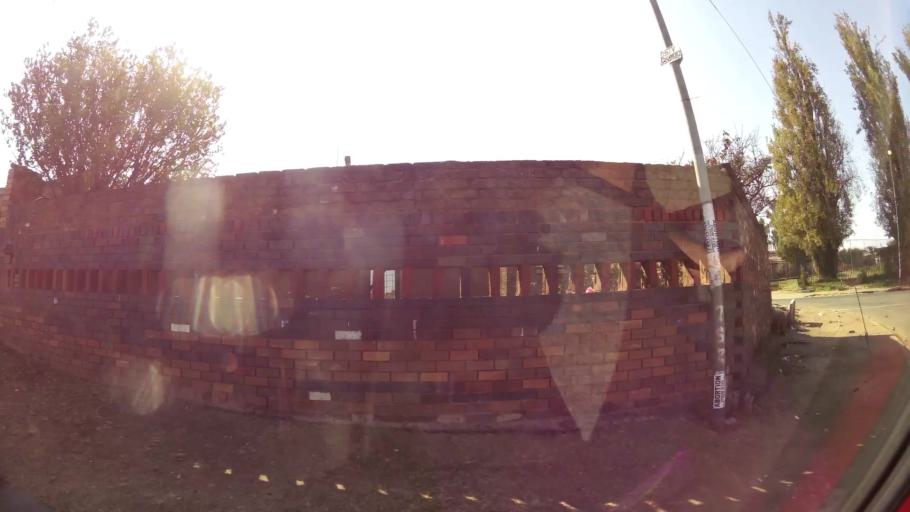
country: ZA
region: Gauteng
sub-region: City of Johannesburg Metropolitan Municipality
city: Soweto
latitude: -26.2483
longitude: 27.9366
